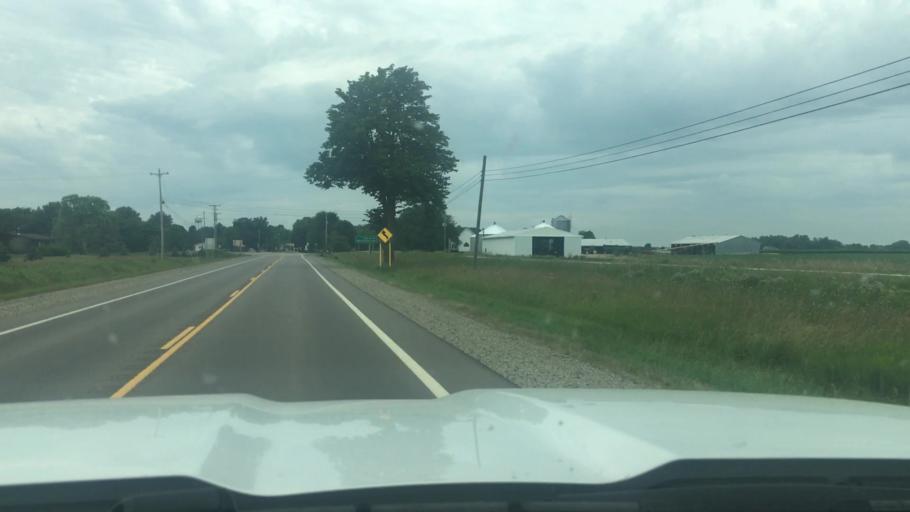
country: US
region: Michigan
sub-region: Clinton County
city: Fowler
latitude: 43.0017
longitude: -84.8335
